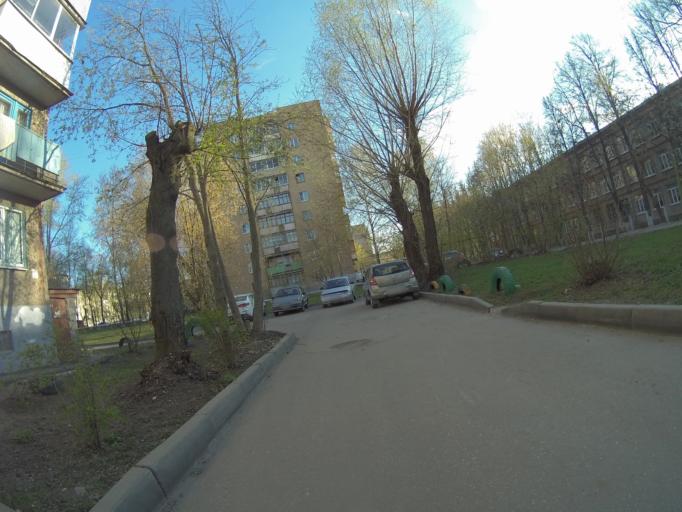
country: RU
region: Vladimir
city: Vladimir
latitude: 56.1400
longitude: 40.3623
